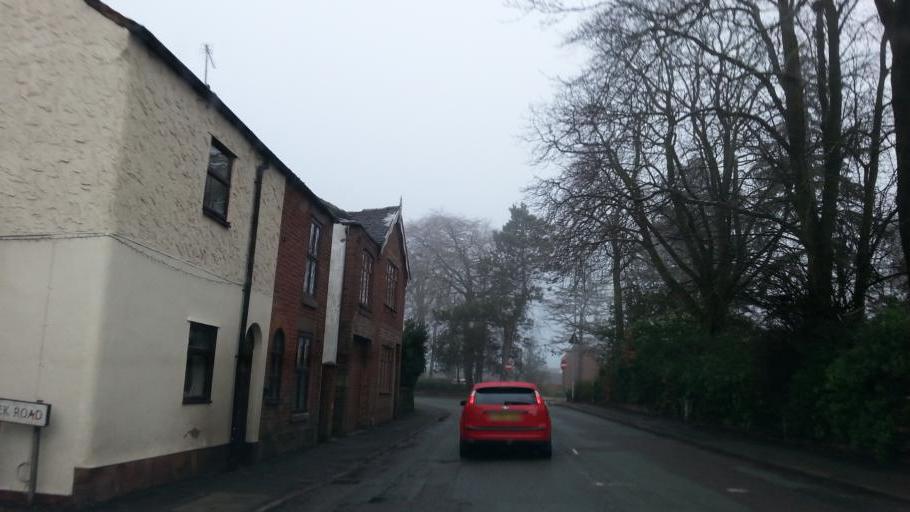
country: GB
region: England
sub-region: Cheshire East
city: Congleton
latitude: 53.1536
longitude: -2.1843
